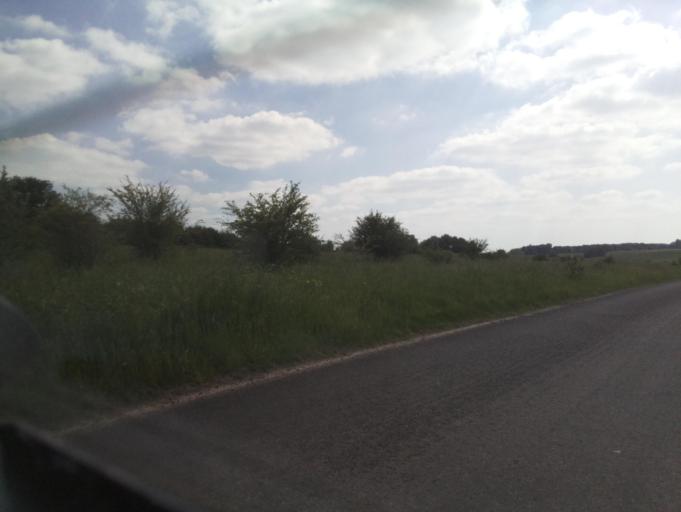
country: GB
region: England
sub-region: Wiltshire
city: Tidworth
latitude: 51.2682
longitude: -1.7197
